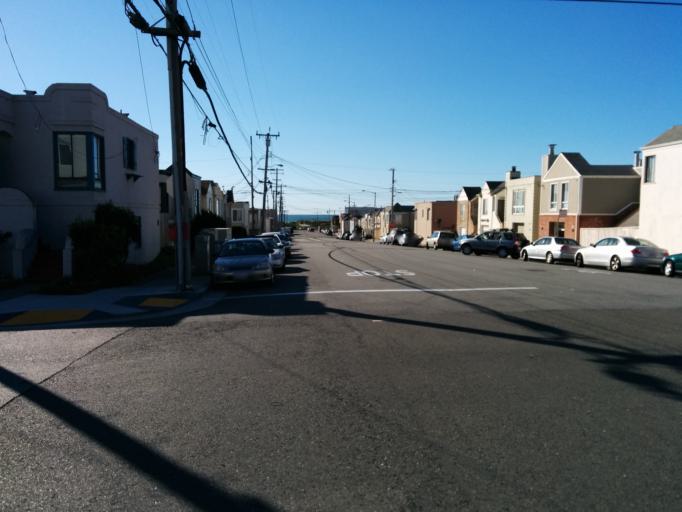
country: US
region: California
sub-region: San Mateo County
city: Daly City
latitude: 37.7380
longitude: -122.5033
